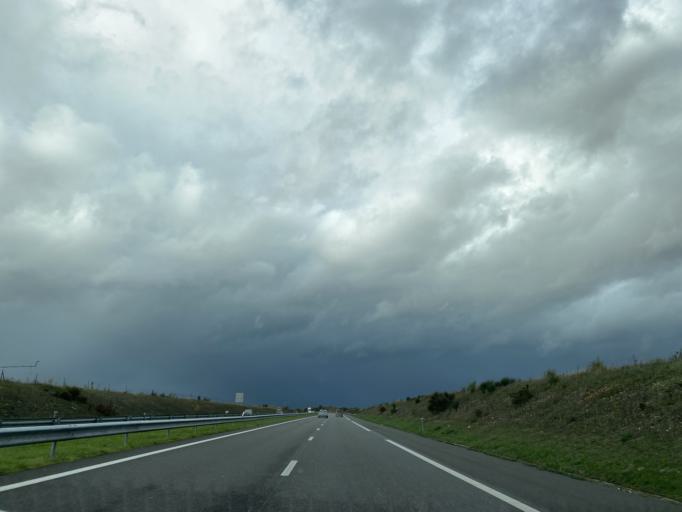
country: FR
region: Centre
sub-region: Departement du Cher
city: Plaimpied-Givaudins
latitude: 46.9925
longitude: 2.4082
